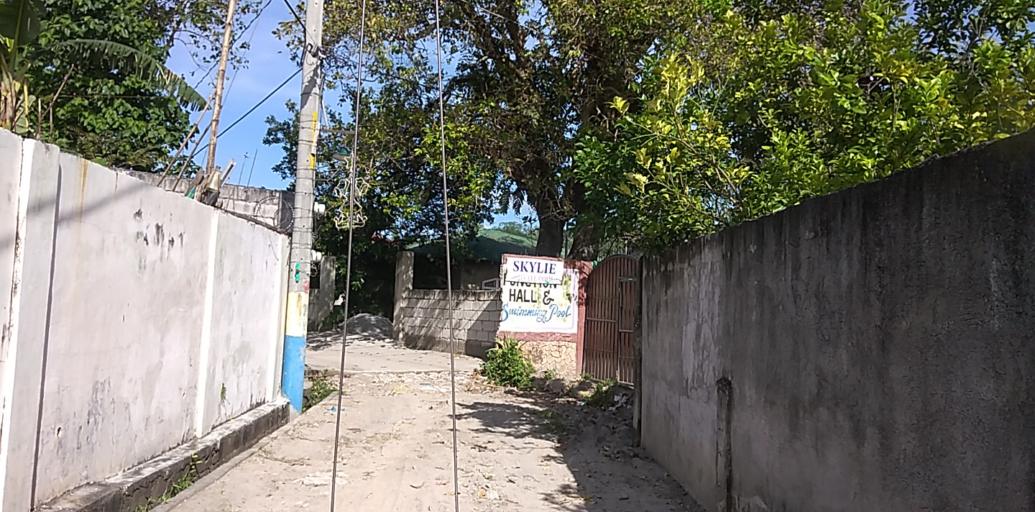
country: PH
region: Central Luzon
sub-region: Province of Pampanga
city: Porac
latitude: 15.0787
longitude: 120.5387
